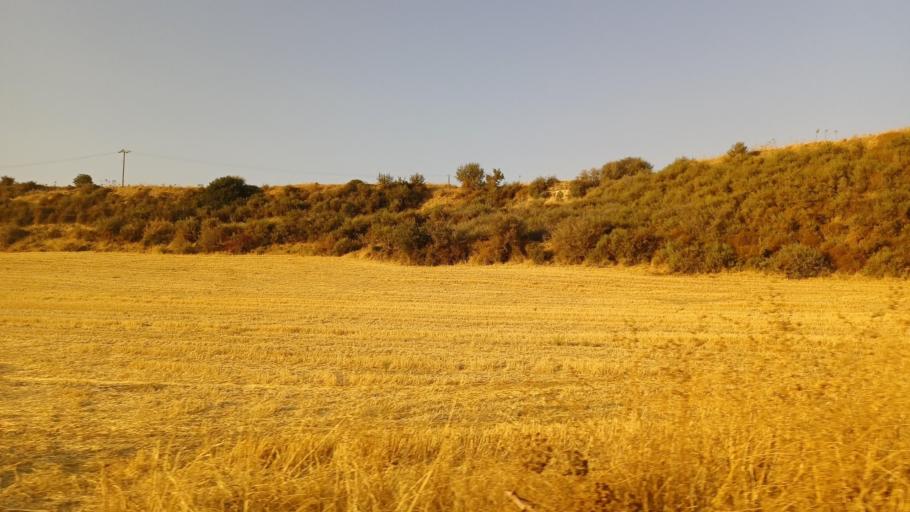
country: CY
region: Pafos
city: Polis
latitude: 35.0456
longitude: 32.4605
